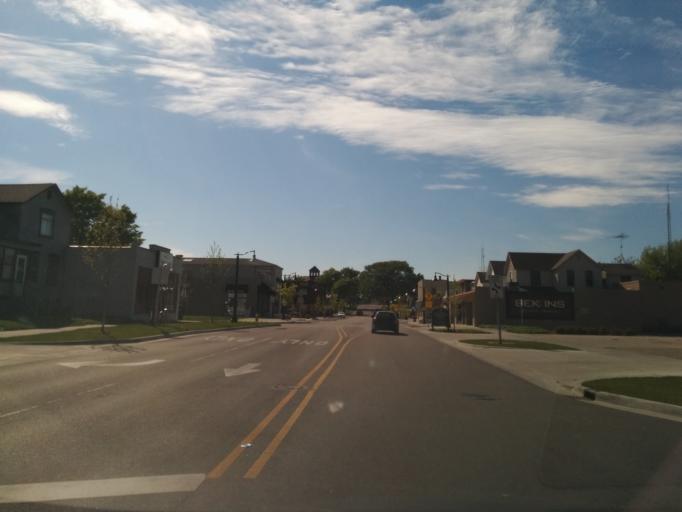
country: US
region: Michigan
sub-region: Ottawa County
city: Grand Haven
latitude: 43.0609
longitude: -86.2209
